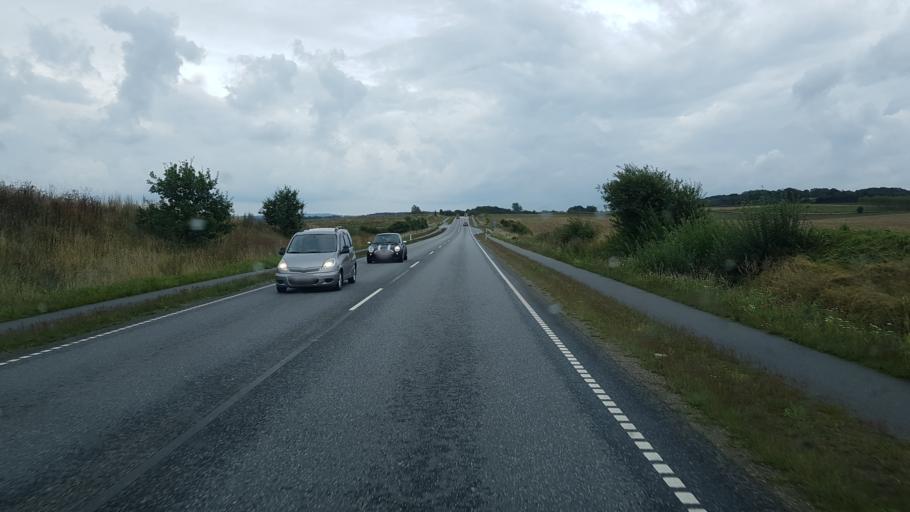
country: DK
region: Central Jutland
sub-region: Horsens Kommune
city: Horsens
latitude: 55.9059
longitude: 9.7355
